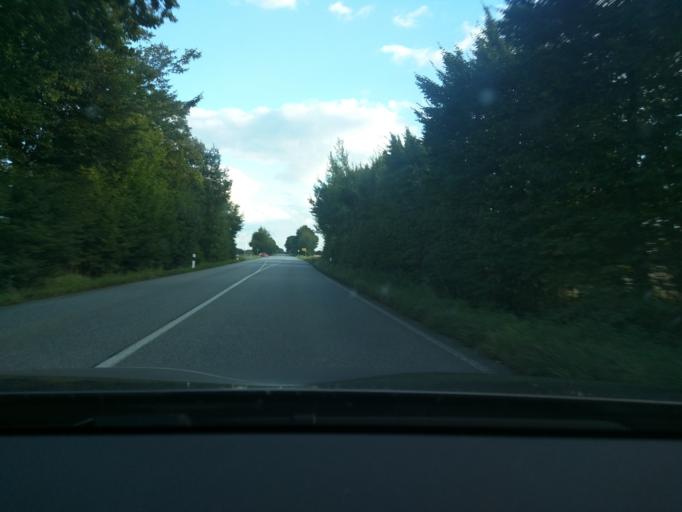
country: DE
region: Schleswig-Holstein
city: Schulendorf
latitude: 53.4745
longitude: 10.5341
